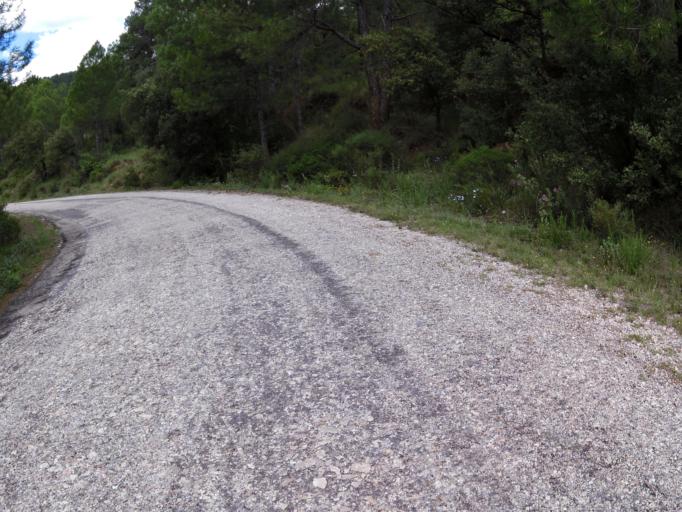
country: ES
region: Castille-La Mancha
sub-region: Provincia de Albacete
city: Paterna del Madera
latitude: 38.5799
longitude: -2.3438
